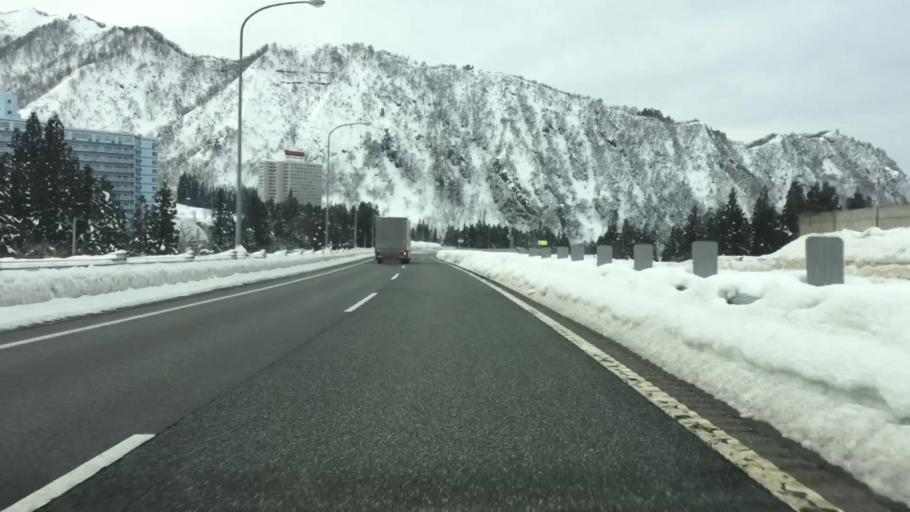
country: JP
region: Niigata
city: Shiozawa
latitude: 36.9066
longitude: 138.8448
